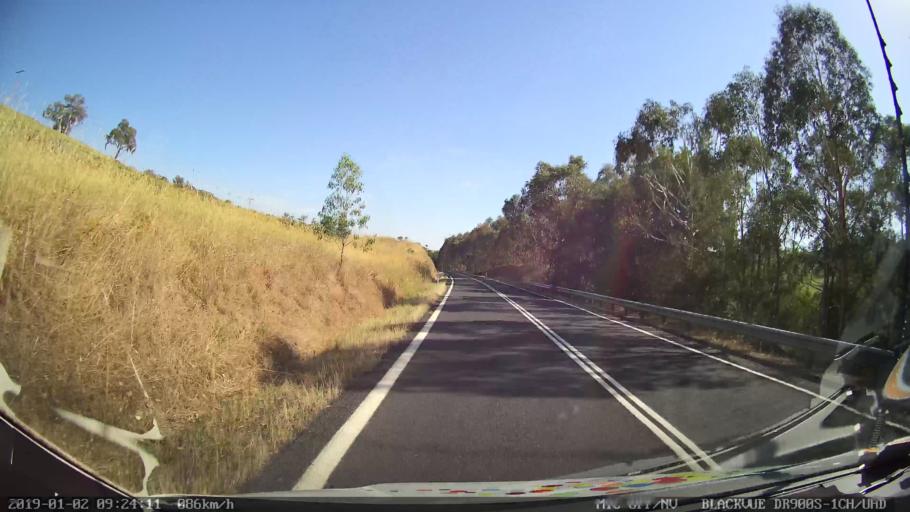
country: AU
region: New South Wales
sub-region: Tumut Shire
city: Tumut
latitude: -35.3804
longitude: 148.2919
